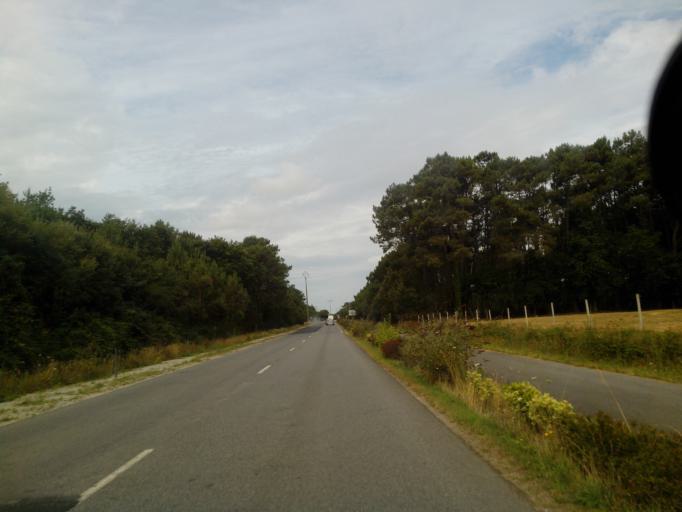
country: FR
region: Brittany
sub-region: Departement du Morbihan
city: Ploemel
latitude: 47.6427
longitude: -3.1050
